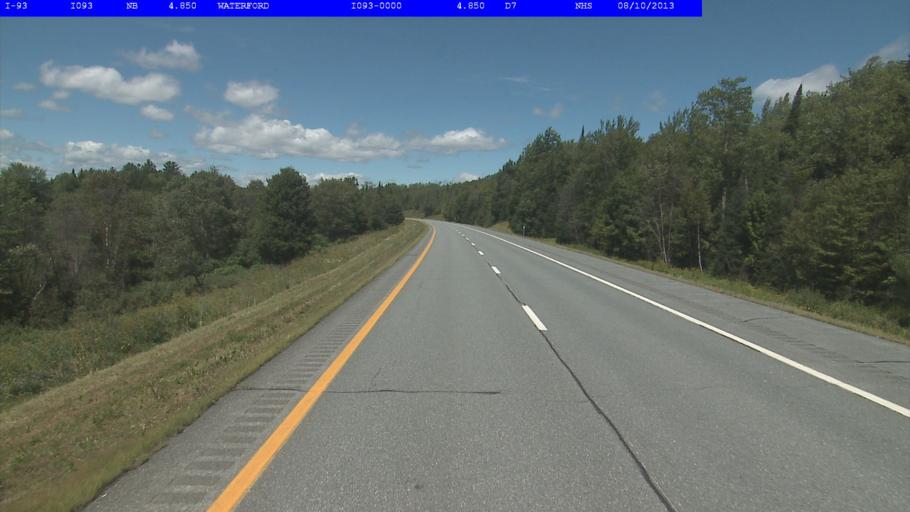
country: US
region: Vermont
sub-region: Caledonia County
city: Saint Johnsbury
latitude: 44.4054
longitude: -71.9187
